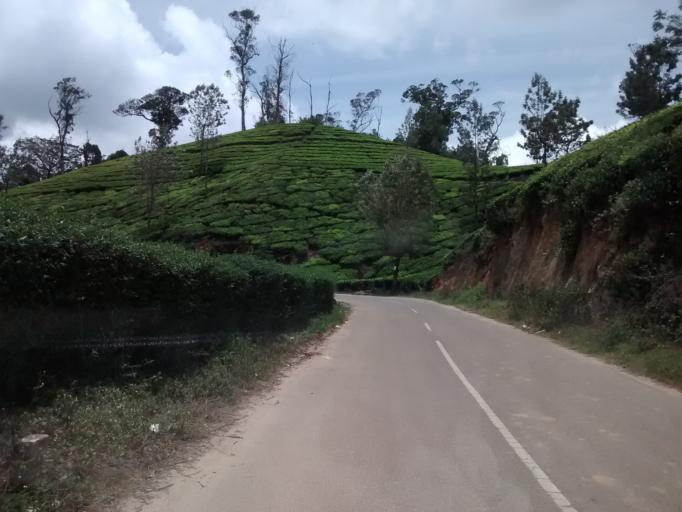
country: IN
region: Tamil Nadu
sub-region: Theni
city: Bodinayakkanur
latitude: 10.1290
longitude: 77.2348
